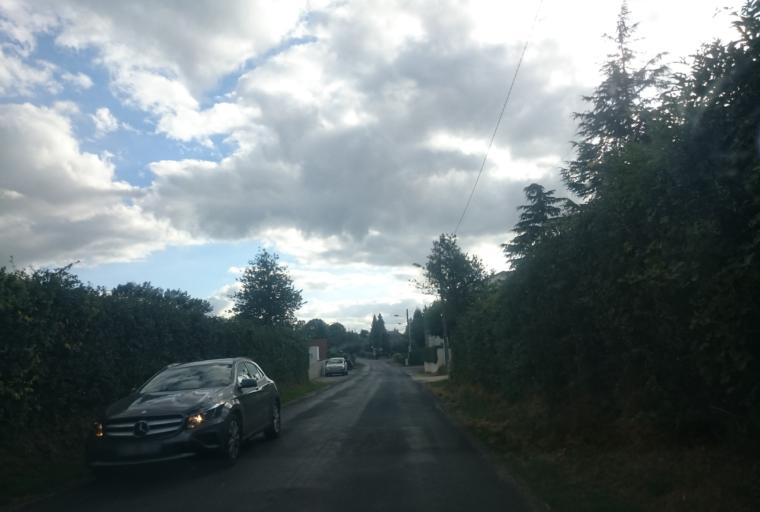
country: FR
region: Auvergne
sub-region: Departement du Cantal
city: Saint-Mamet-la-Salvetat
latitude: 44.8588
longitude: 2.2984
